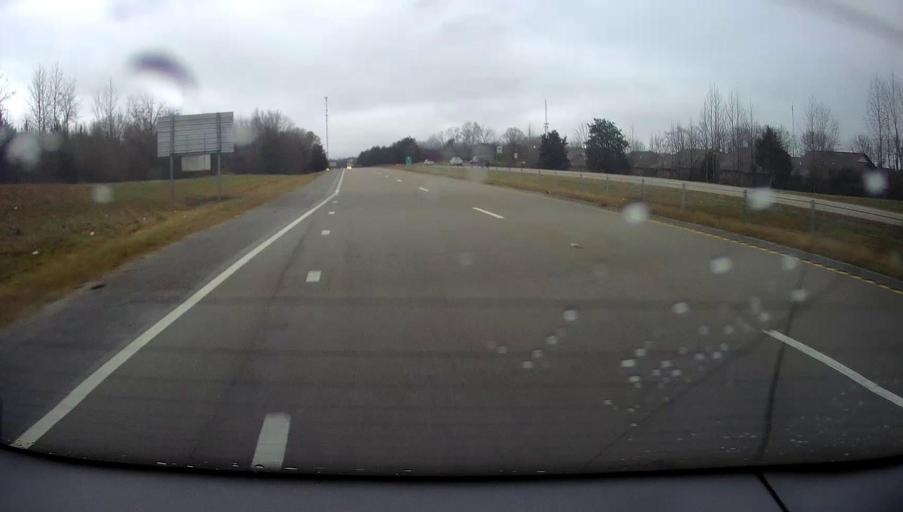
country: US
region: Mississippi
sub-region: Alcorn County
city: Corinth
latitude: 34.9121
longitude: -88.5436
